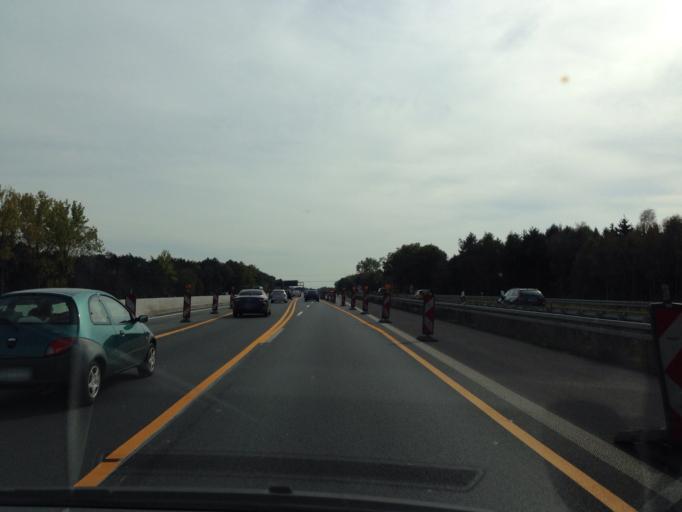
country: DE
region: North Rhine-Westphalia
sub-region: Regierungsbezirk Munster
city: Muenster
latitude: 51.9120
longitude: 7.5620
